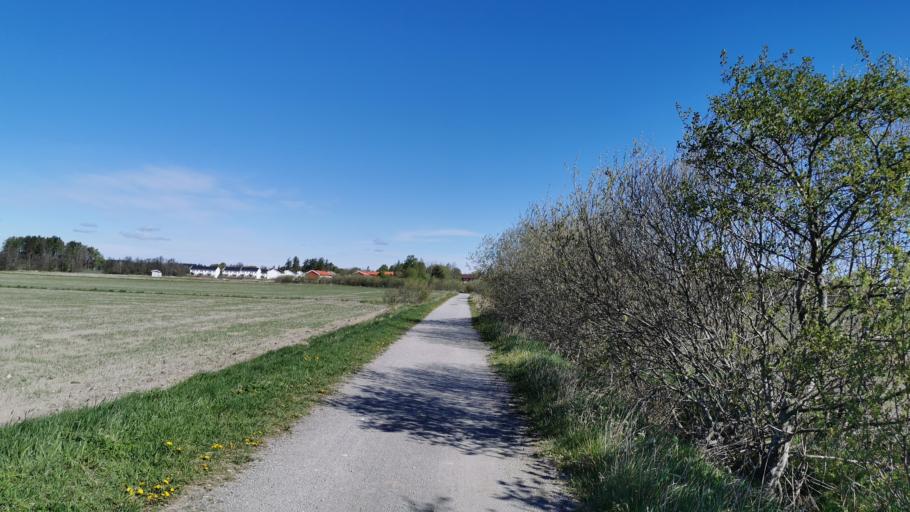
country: SE
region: OErebro
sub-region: Orebro Kommun
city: Orebro
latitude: 59.3096
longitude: 15.2160
